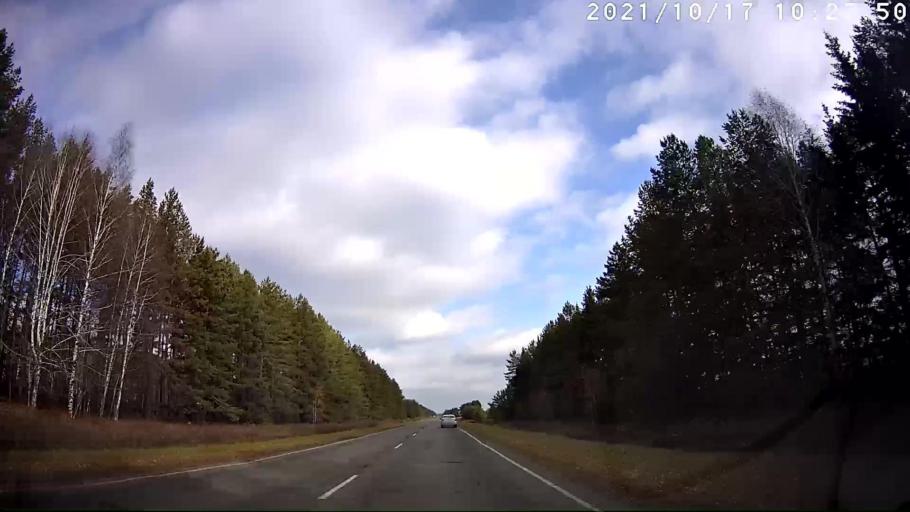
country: RU
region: Mariy-El
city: Kuzhener
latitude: 56.8377
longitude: 48.7349
